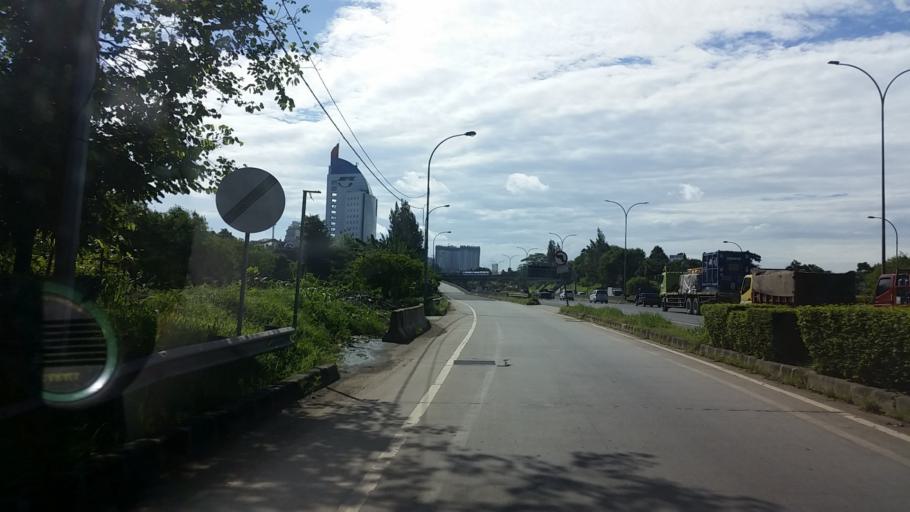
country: ID
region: Banten
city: South Tangerang
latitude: -6.2769
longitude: 106.7687
